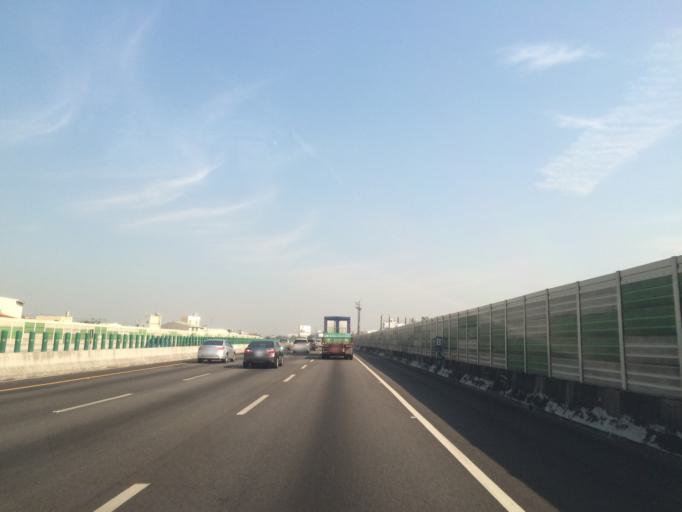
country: TW
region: Taiwan
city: Fengyuan
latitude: 24.2217
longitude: 120.6813
